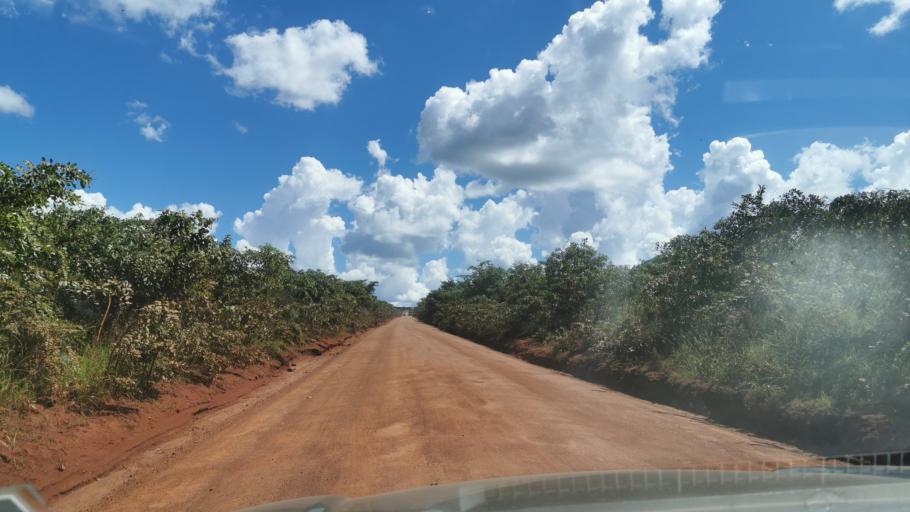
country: TZ
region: Kagera
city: Biharamulo
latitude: -2.9865
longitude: 31.2195
